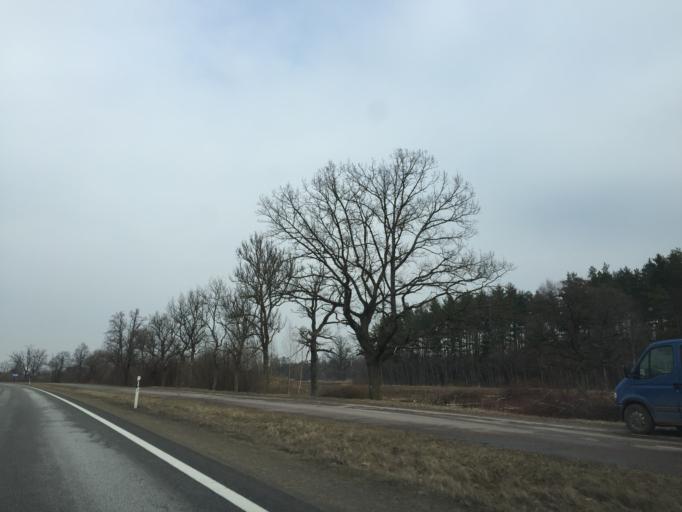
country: LV
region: Salacgrivas
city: Salacgriva
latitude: 57.6855
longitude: 24.3822
